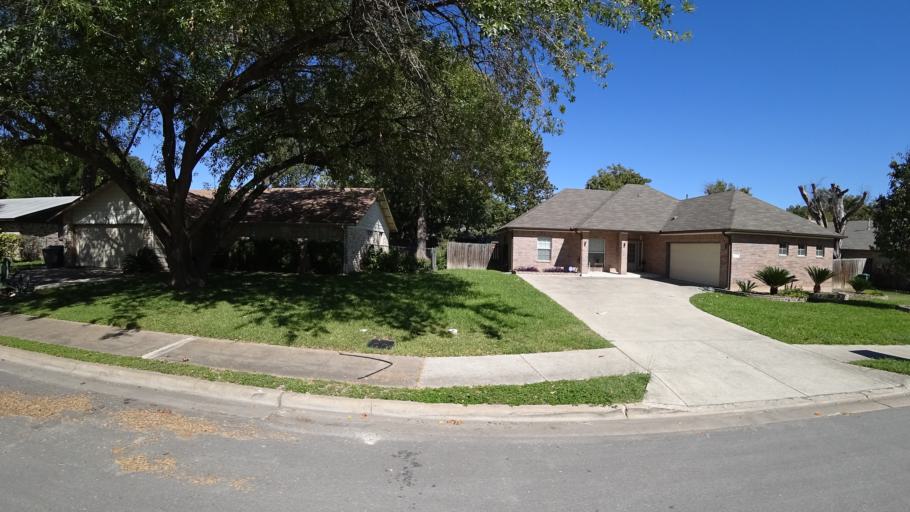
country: US
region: Texas
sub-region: Travis County
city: Hornsby Bend
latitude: 30.3045
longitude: -97.6543
